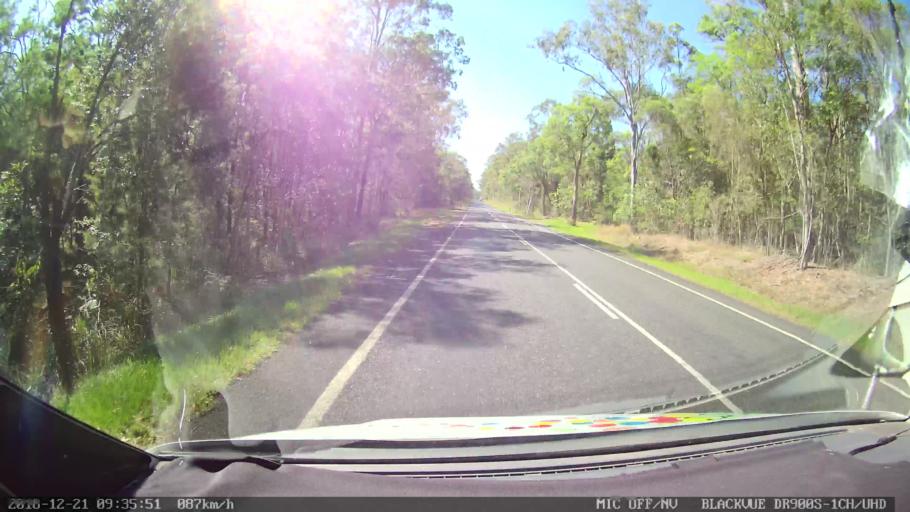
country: AU
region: New South Wales
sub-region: Clarence Valley
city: Grafton
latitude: -29.5159
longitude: 152.9806
